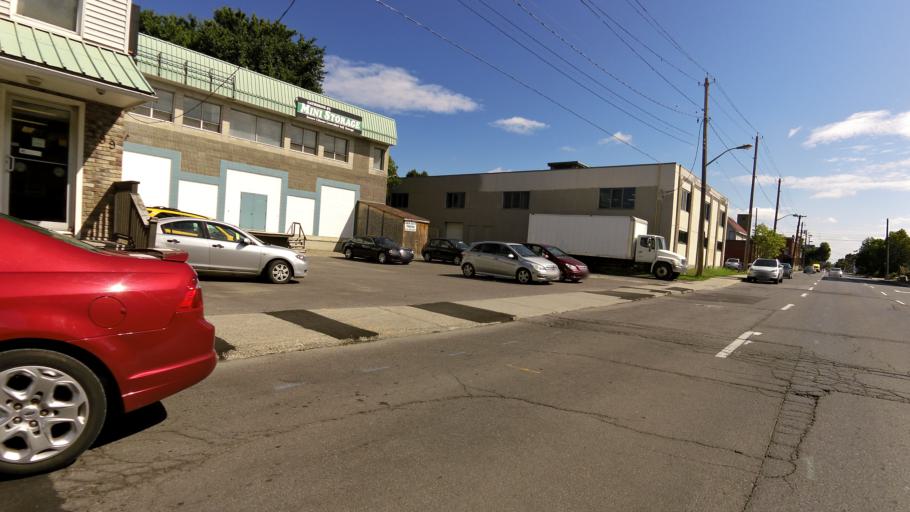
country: CA
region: Ontario
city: Ottawa
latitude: 45.4068
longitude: -75.6986
